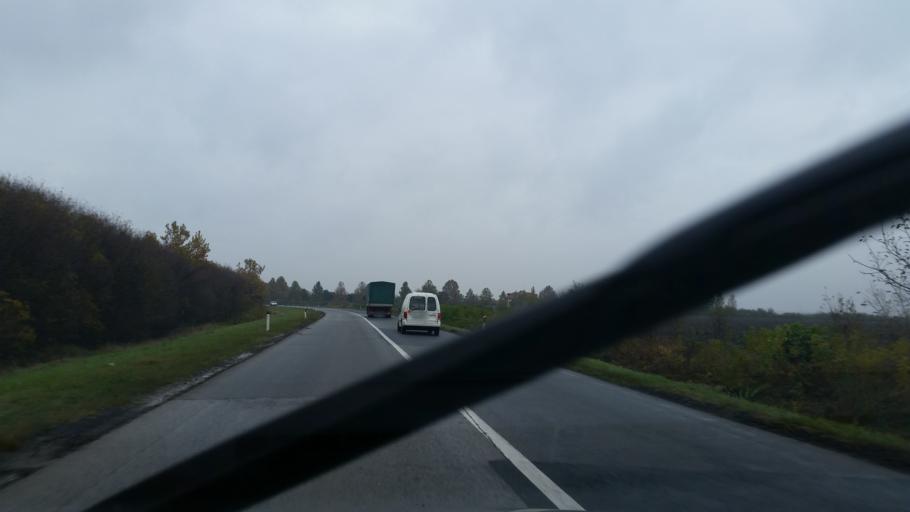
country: RS
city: Sefkerin
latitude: 44.9498
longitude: 20.4323
